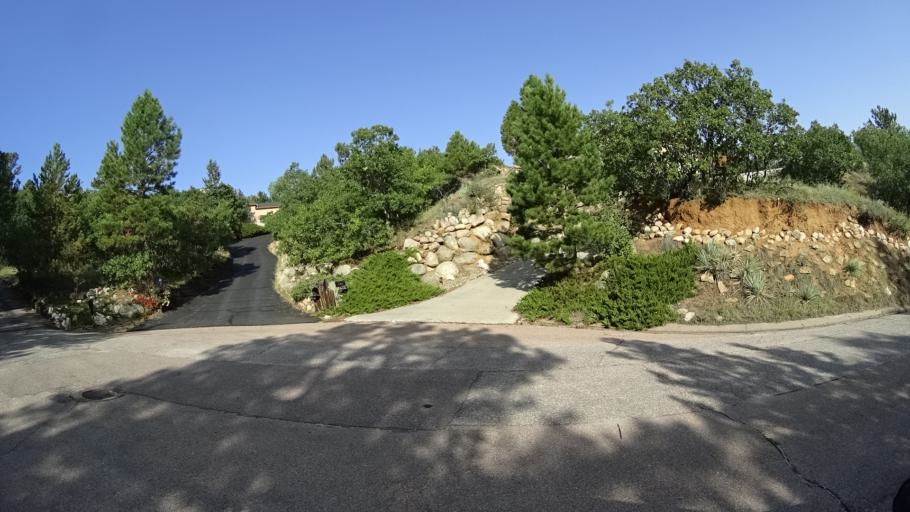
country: US
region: Colorado
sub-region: El Paso County
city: Colorado Springs
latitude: 38.8188
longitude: -104.8719
